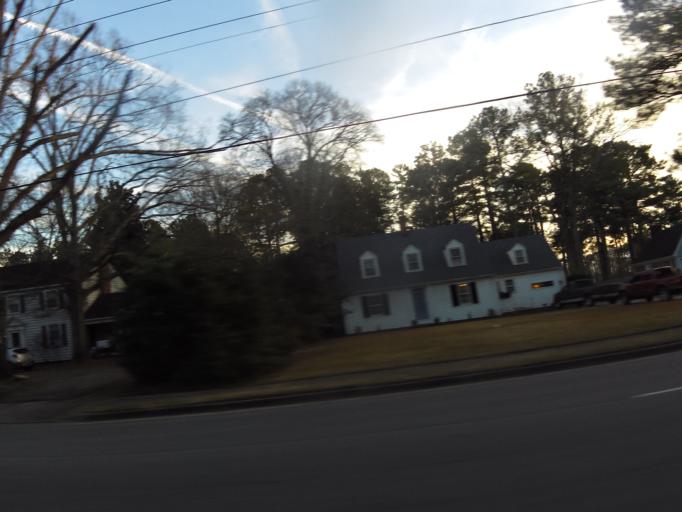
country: US
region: Virginia
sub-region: City of Franklin
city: Franklin
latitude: 36.6833
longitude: -76.9456
